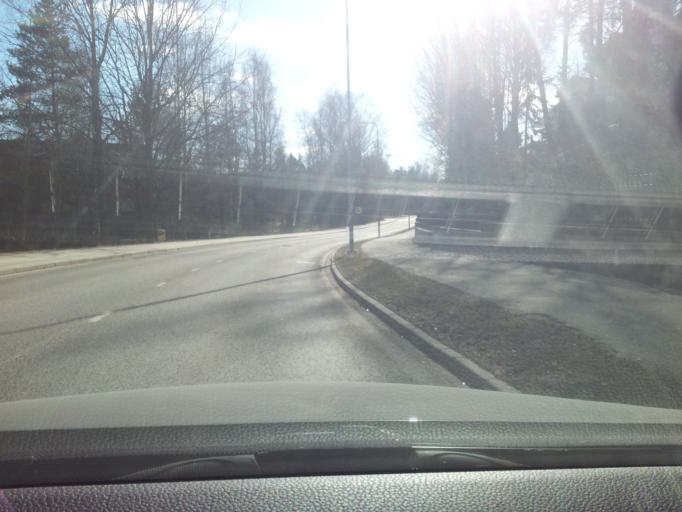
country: FI
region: Uusimaa
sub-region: Helsinki
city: Koukkuniemi
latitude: 60.1621
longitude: 24.7911
